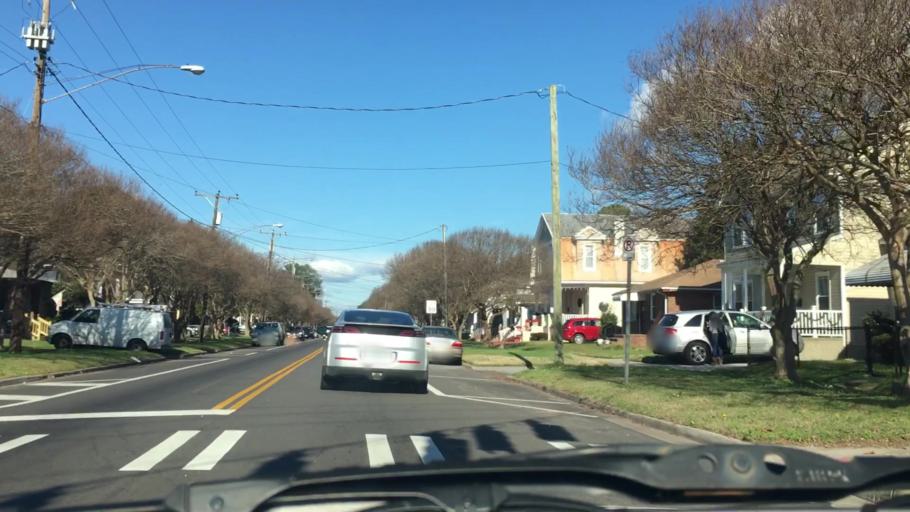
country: US
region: Virginia
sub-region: City of Norfolk
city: Norfolk
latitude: 36.8679
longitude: -76.2516
